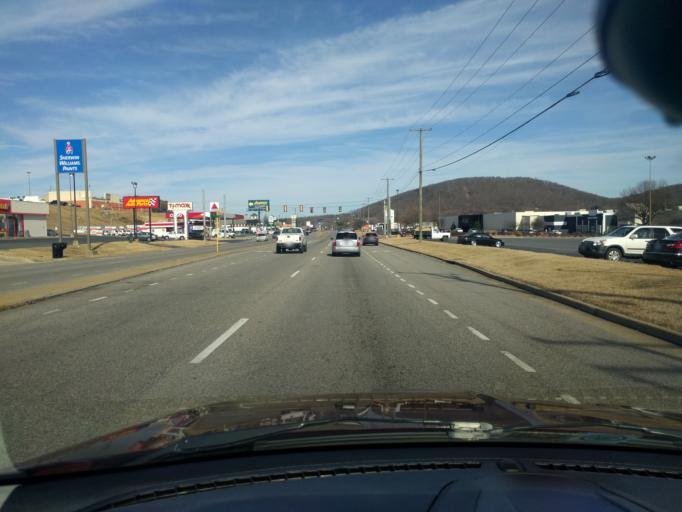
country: US
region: Virginia
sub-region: Augusta County
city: Jolivue
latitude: 38.1240
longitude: -79.0652
